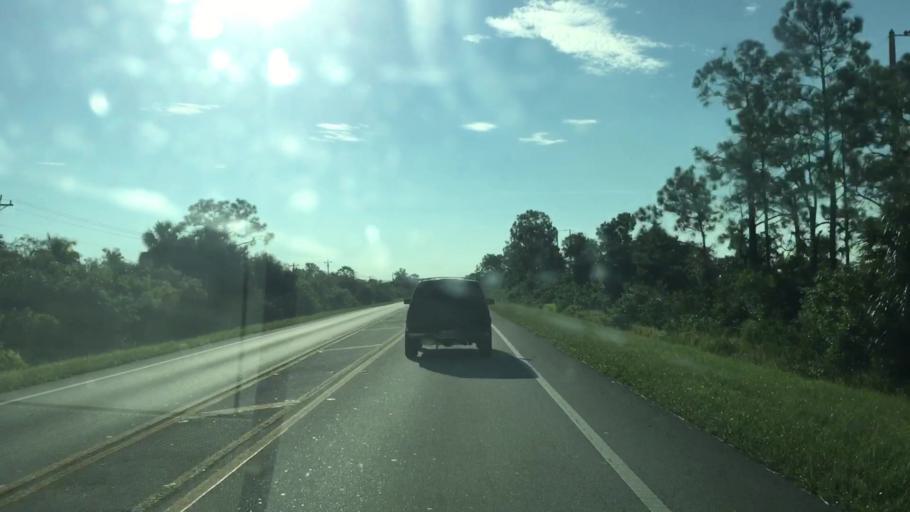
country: US
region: Florida
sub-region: Collier County
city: Immokalee
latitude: 26.5095
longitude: -81.5321
